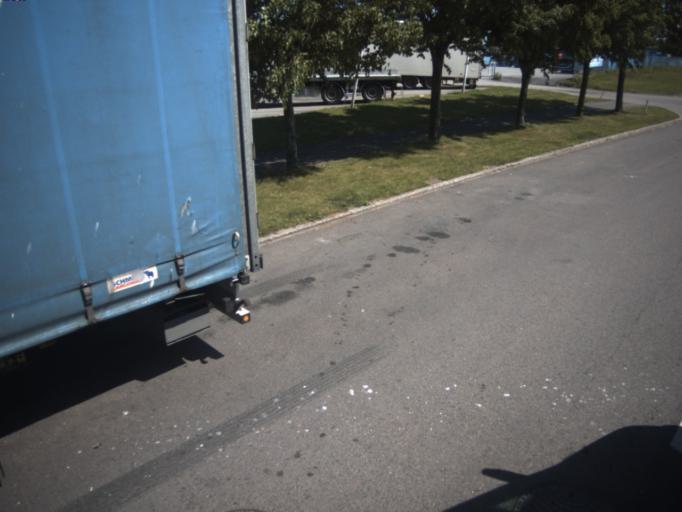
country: SE
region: Skane
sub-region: Helsingborg
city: Gantofta
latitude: 56.0052
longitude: 12.7714
